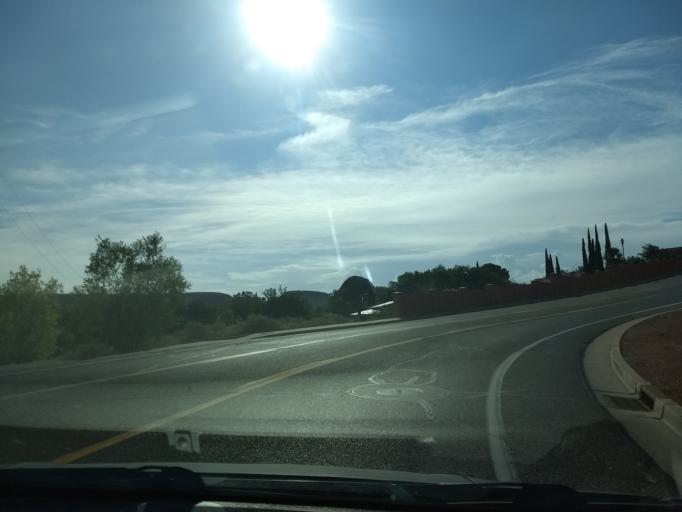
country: US
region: Utah
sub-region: Washington County
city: Saint George
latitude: 37.1140
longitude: -113.5799
